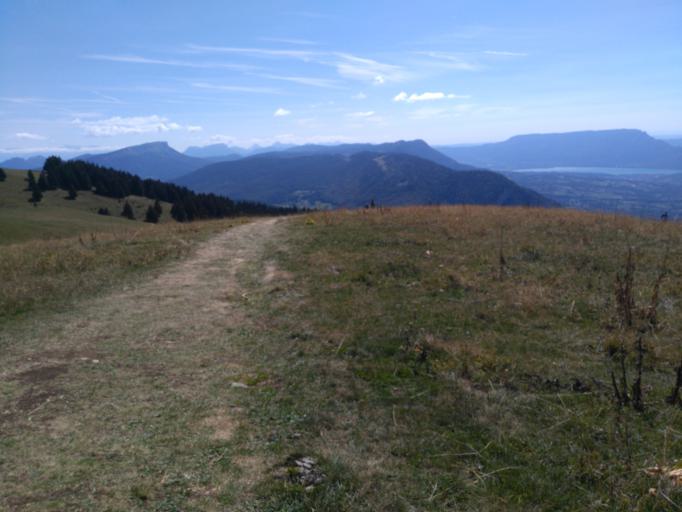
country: FR
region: Rhone-Alpes
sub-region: Departement de la Haute-Savoie
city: Gruffy
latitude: 45.7799
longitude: 6.0897
